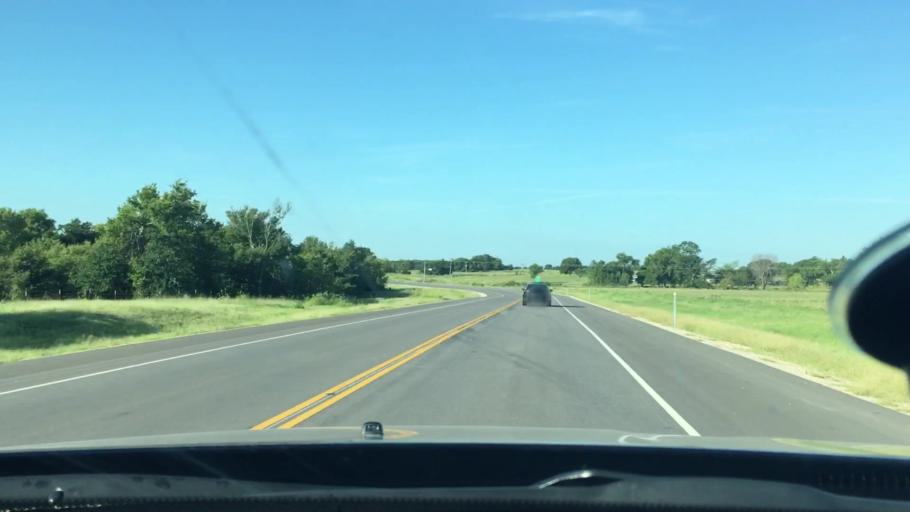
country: US
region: Oklahoma
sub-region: Johnston County
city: Tishomingo
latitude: 34.3213
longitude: -96.6677
